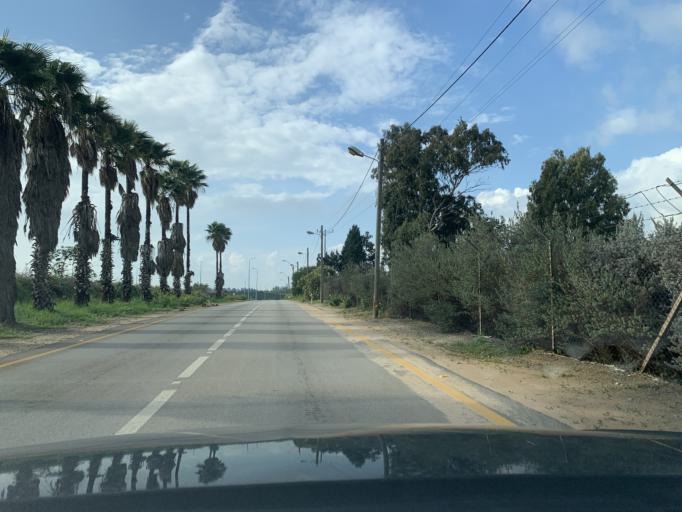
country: PS
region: West Bank
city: Qalqilyah
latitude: 32.1958
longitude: 34.9445
